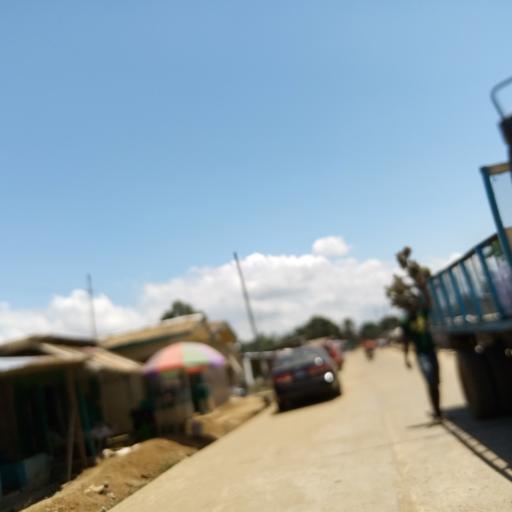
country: LR
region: Montserrado
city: Monrovia
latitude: 6.2425
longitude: -10.6949
